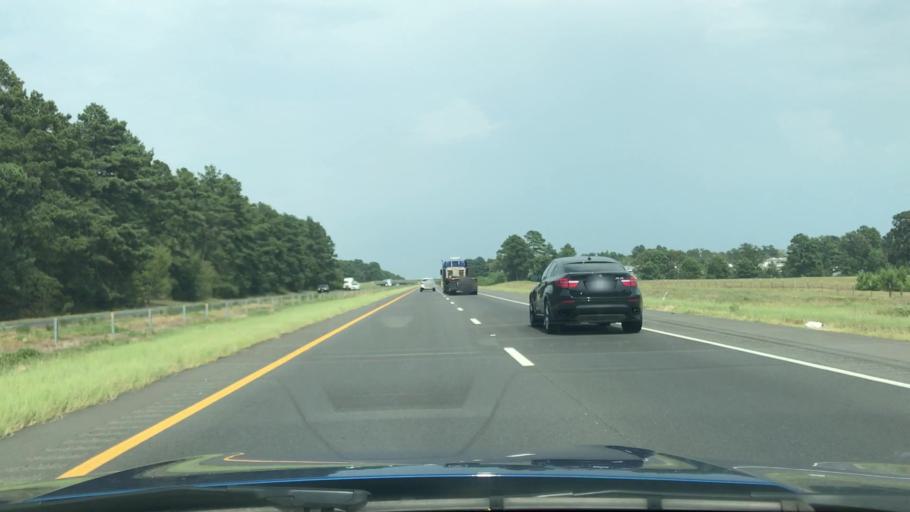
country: US
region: Texas
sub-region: Harrison County
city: Hallsville
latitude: 32.4655
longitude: -94.6297
